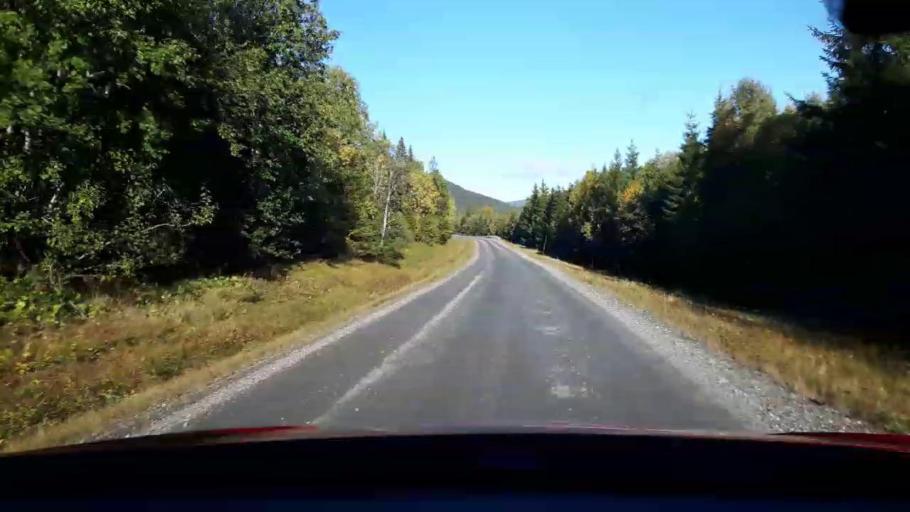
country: NO
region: Nord-Trondelag
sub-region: Lierne
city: Sandvika
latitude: 64.5832
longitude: 13.8877
